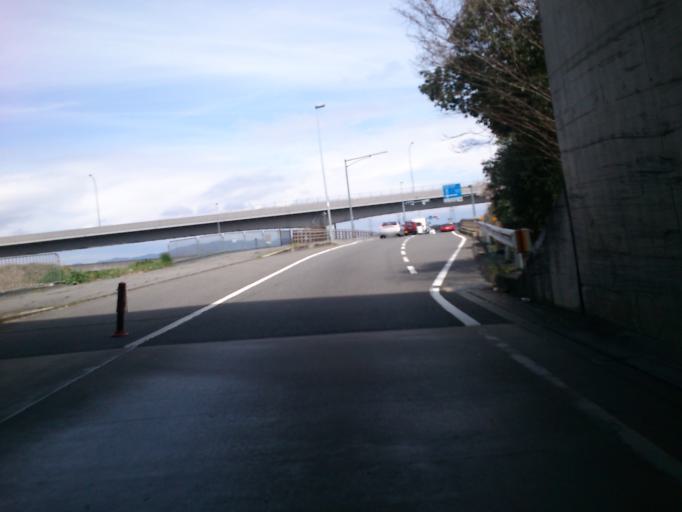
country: JP
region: Nara
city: Nara-shi
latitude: 34.7190
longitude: 135.8121
